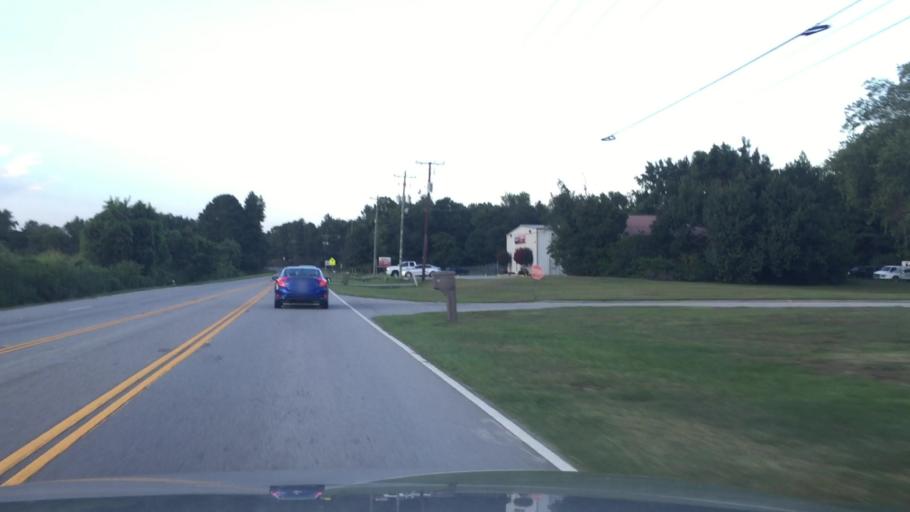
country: US
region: South Carolina
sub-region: Richland County
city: Hopkins
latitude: 33.9509
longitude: -80.9294
